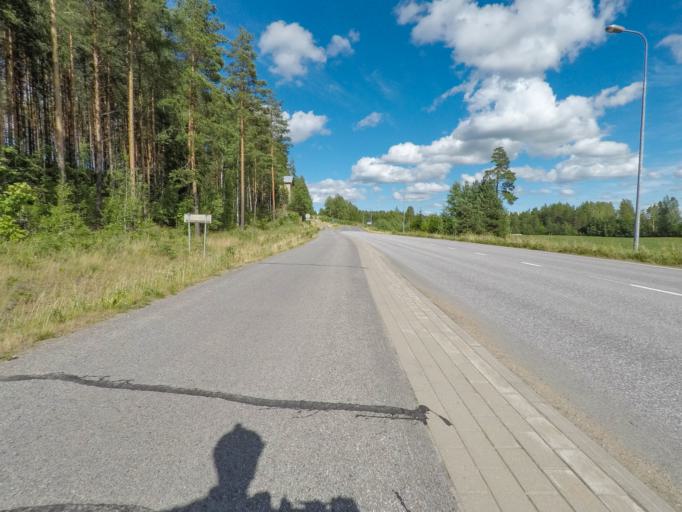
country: FI
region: South Karelia
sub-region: Lappeenranta
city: Lappeenranta
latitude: 61.0858
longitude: 28.3375
